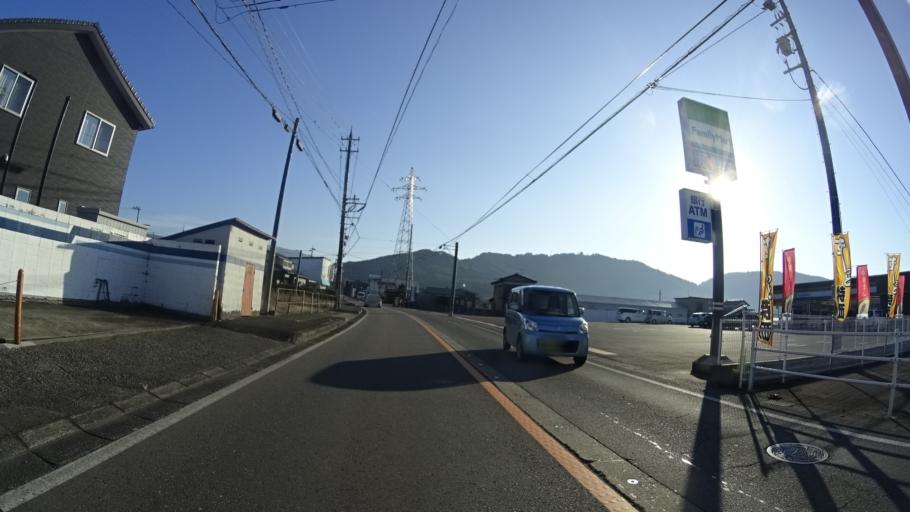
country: JP
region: Fukui
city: Maruoka
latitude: 36.0896
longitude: 136.2884
